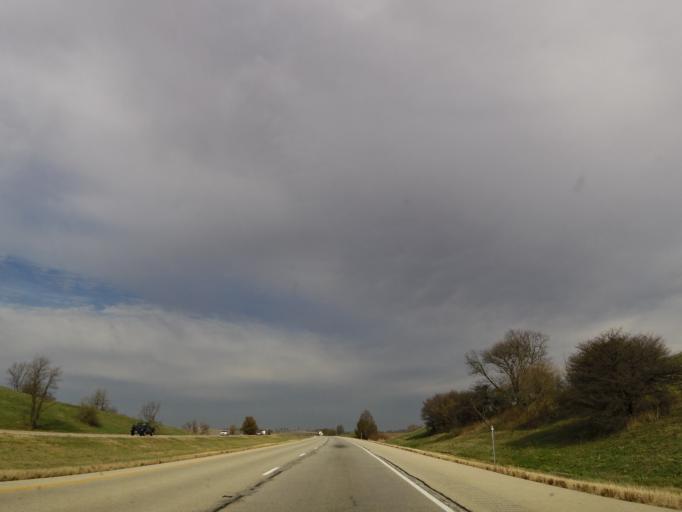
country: US
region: Illinois
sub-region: Henry County
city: Orion
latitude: 41.2459
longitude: -90.3302
